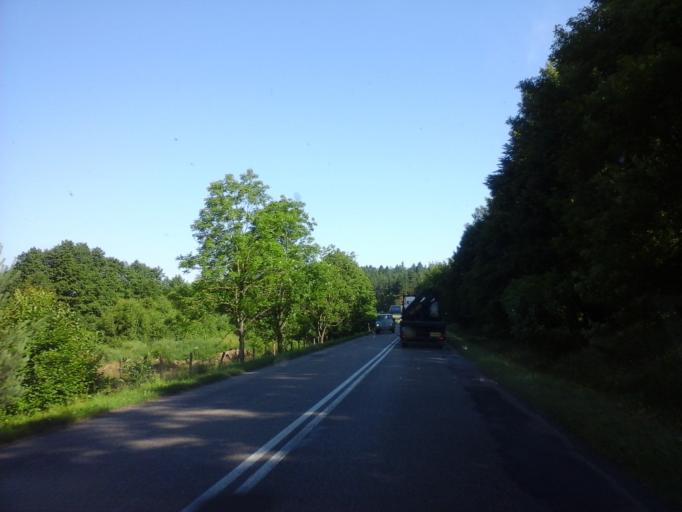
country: PL
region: West Pomeranian Voivodeship
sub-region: Powiat swidwinski
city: Polczyn-Zdroj
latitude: 53.7867
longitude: 16.0726
